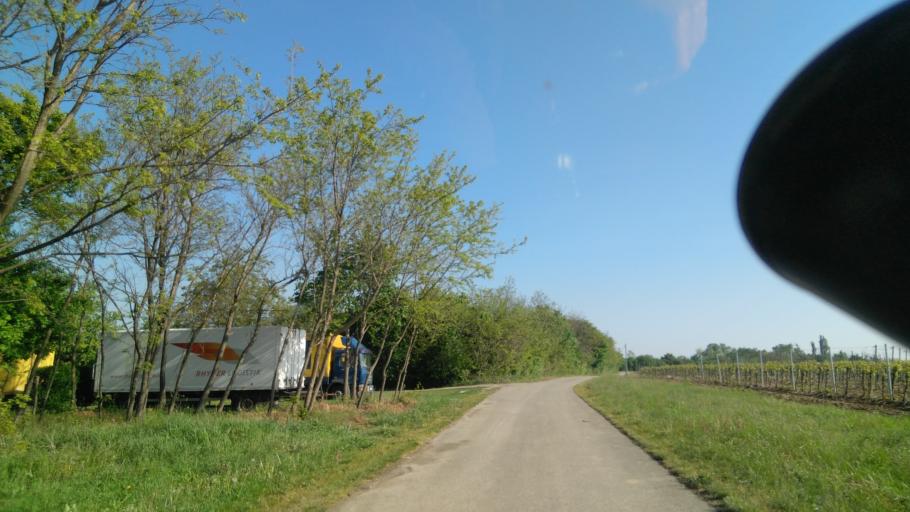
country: HU
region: Zala
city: Sarmellek
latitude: 46.7536
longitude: 17.1412
